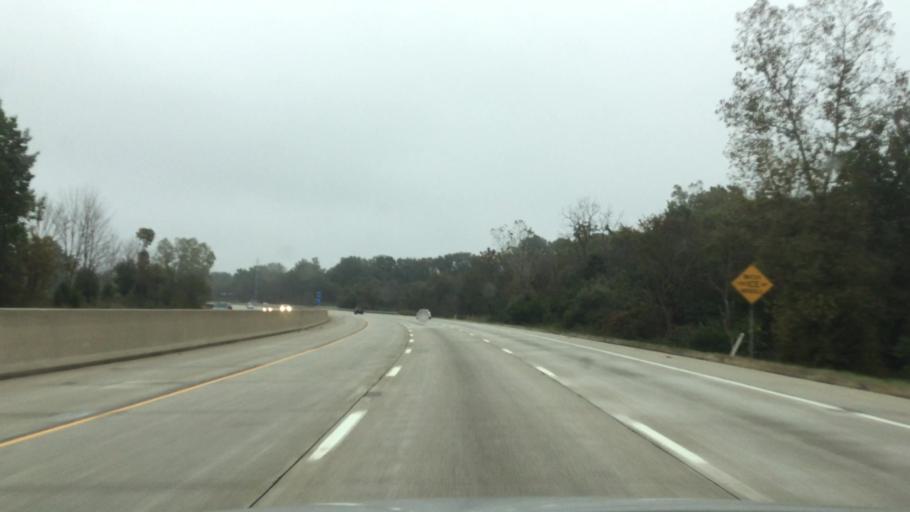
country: US
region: Indiana
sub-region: LaPorte County
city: Trail Creek
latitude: 41.6583
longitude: -86.8755
